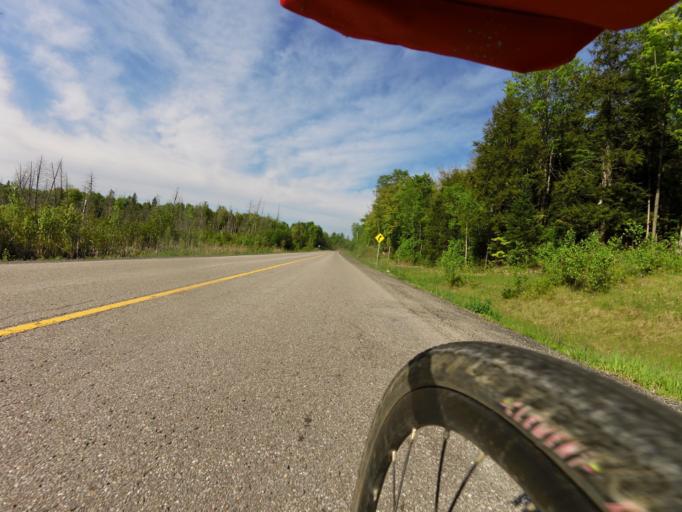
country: CA
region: Ontario
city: Arnprior
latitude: 45.1604
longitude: -76.5080
